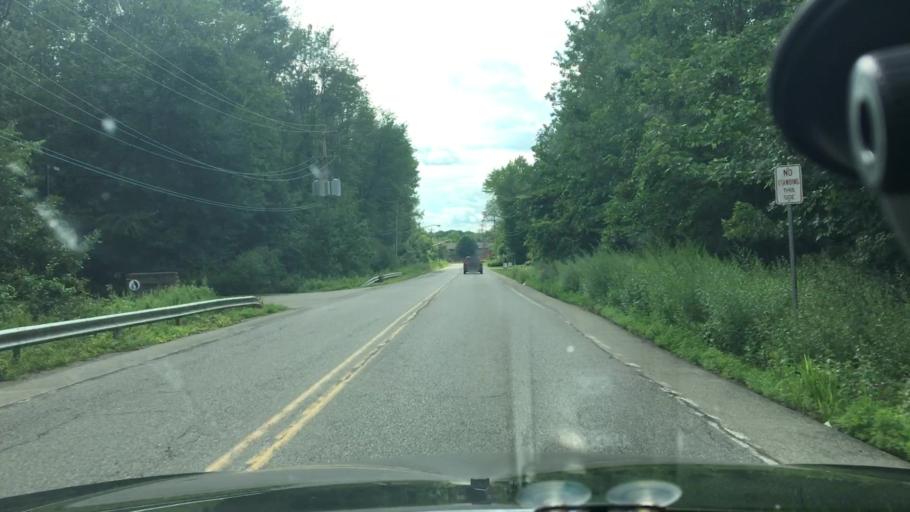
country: US
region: New York
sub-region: Erie County
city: Orchard Park
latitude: 42.7708
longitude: -78.7612
